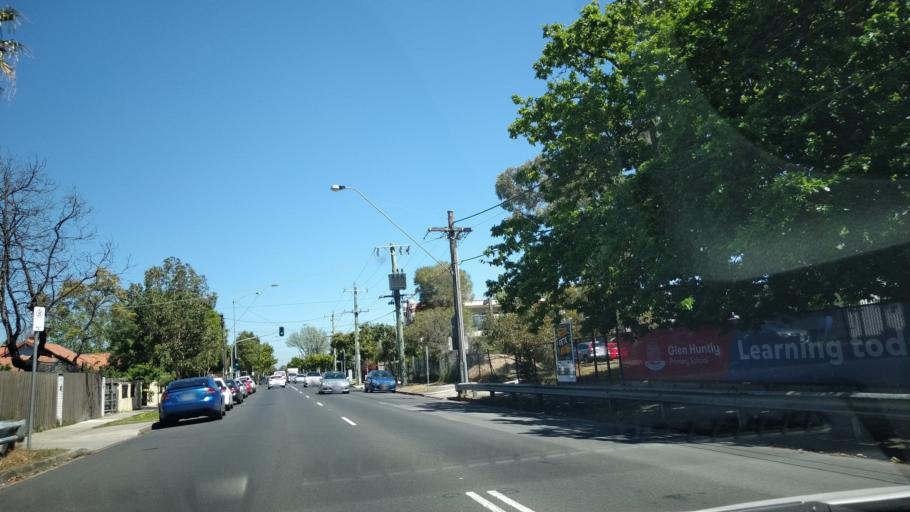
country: AU
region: Victoria
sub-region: Glen Eira
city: Glen Huntly
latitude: -37.8936
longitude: 145.0461
